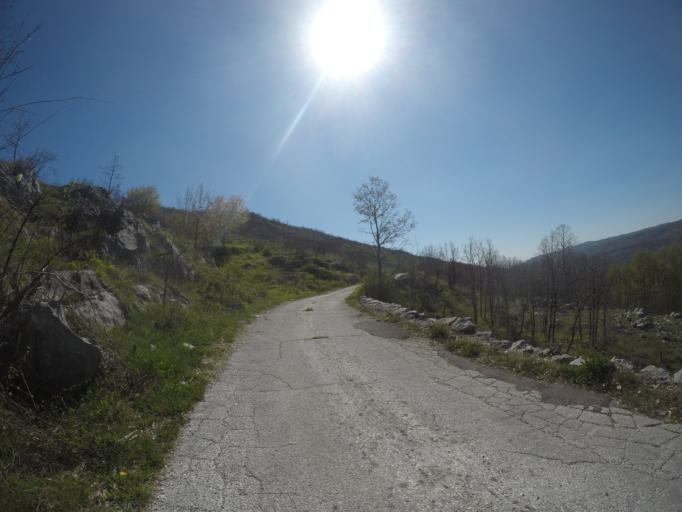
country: ME
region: Danilovgrad
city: Danilovgrad
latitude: 42.5374
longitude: 19.0136
